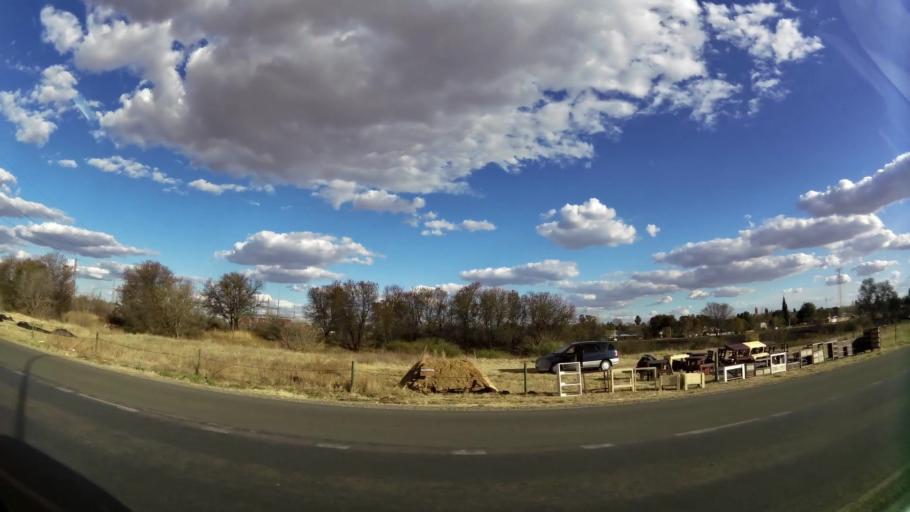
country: ZA
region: North-West
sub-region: Dr Kenneth Kaunda District Municipality
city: Potchefstroom
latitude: -26.7006
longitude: 27.1027
